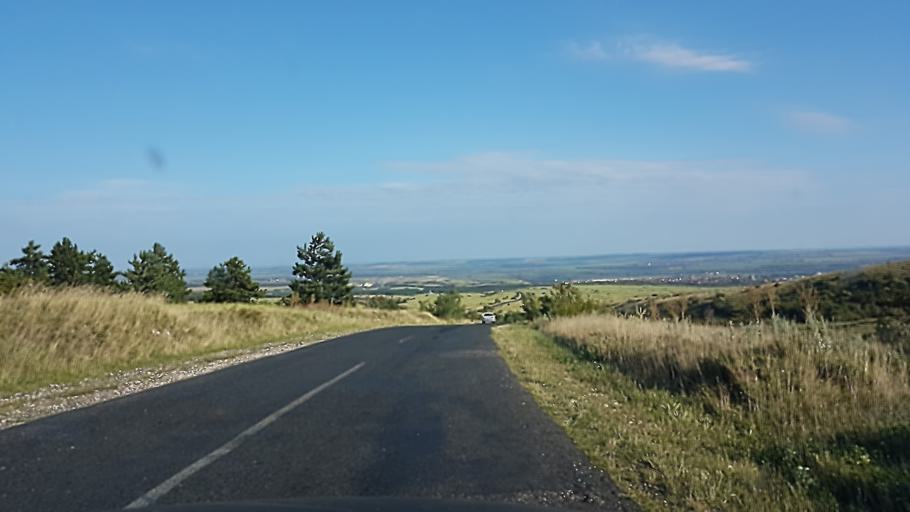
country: HU
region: Veszprem
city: Varpalota
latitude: 47.2349
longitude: 18.1297
